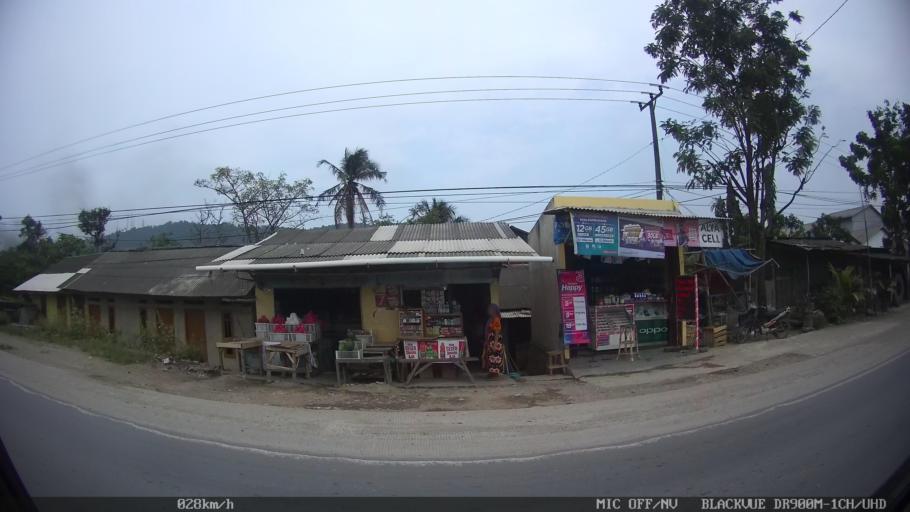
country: ID
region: Lampung
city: Panjang
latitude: -5.4301
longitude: 105.3264
